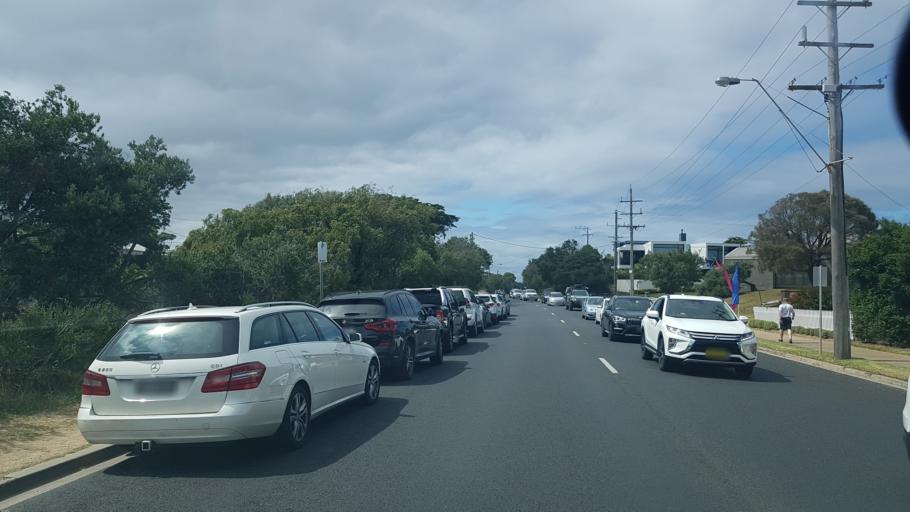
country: AU
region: Victoria
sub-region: Mornington Peninsula
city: Sorrento
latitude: -38.3407
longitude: 144.7368
